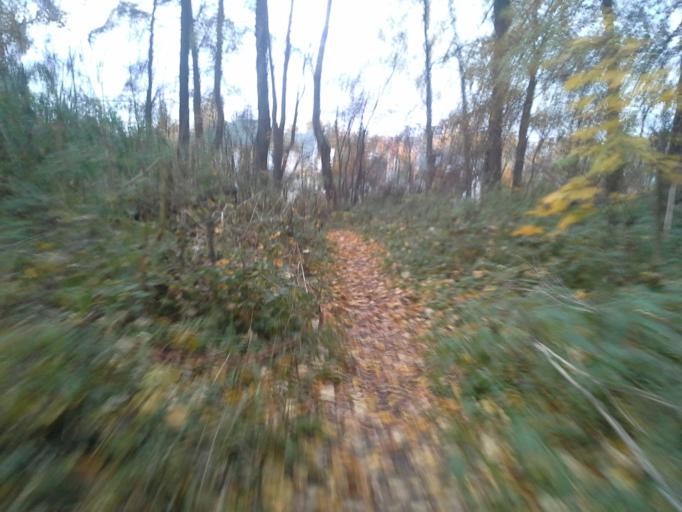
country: RU
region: Moskovskaya
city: Dubrovitsy
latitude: 55.5017
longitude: 37.4395
